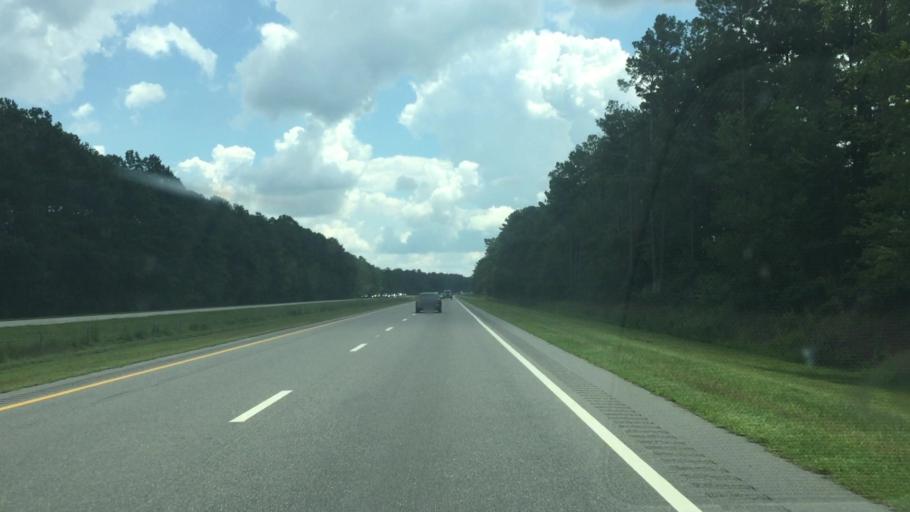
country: US
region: North Carolina
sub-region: Columbus County
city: Chadbourn
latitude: 34.3843
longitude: -78.8652
